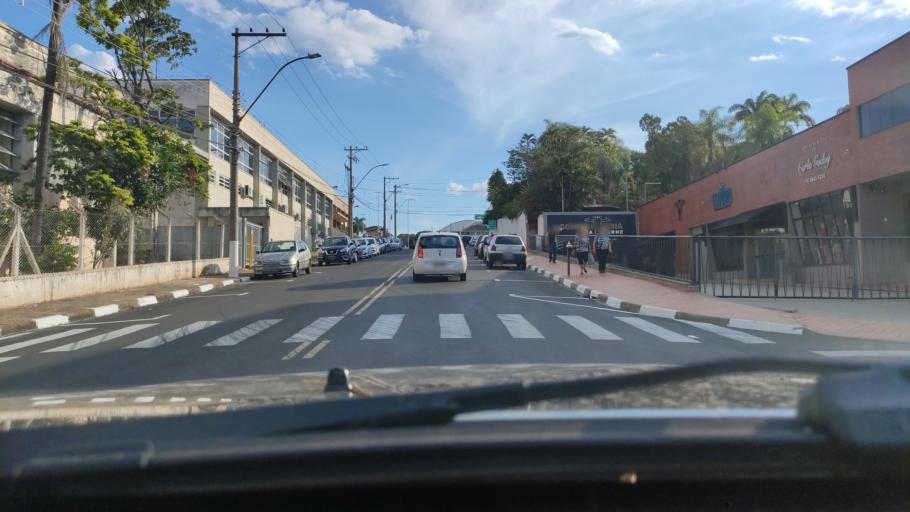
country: BR
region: Sao Paulo
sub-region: Itapira
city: Itapira
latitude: -22.4431
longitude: -46.8301
